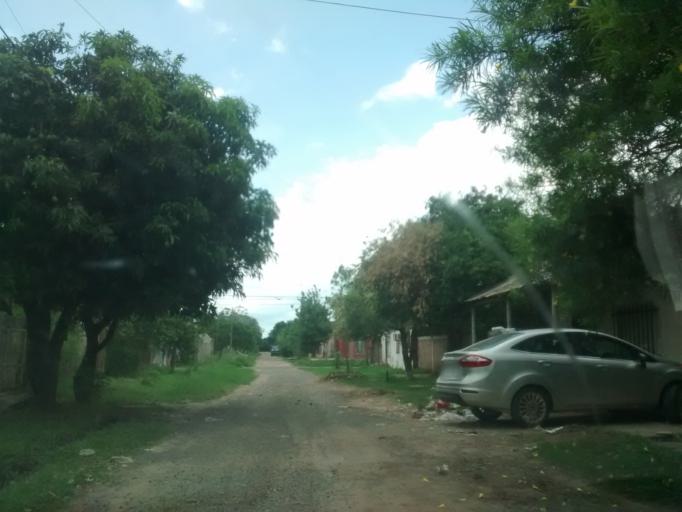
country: AR
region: Chaco
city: Resistencia
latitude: -27.4301
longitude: -58.9788
